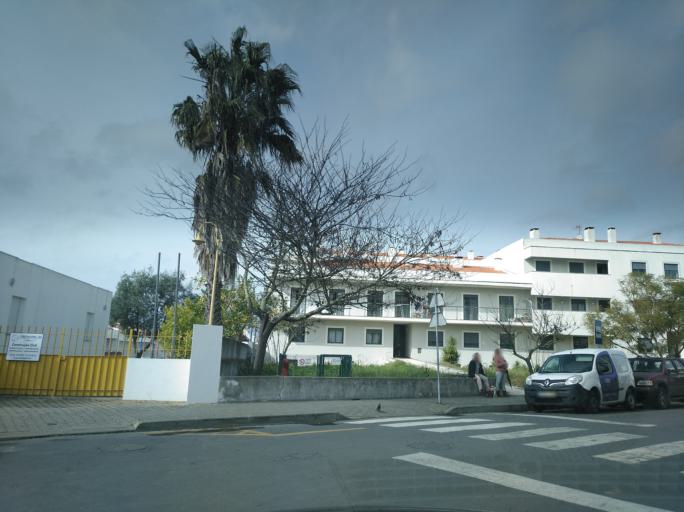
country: PT
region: Setubal
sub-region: Grandola
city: Grandola
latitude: 38.1776
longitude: -8.5621
